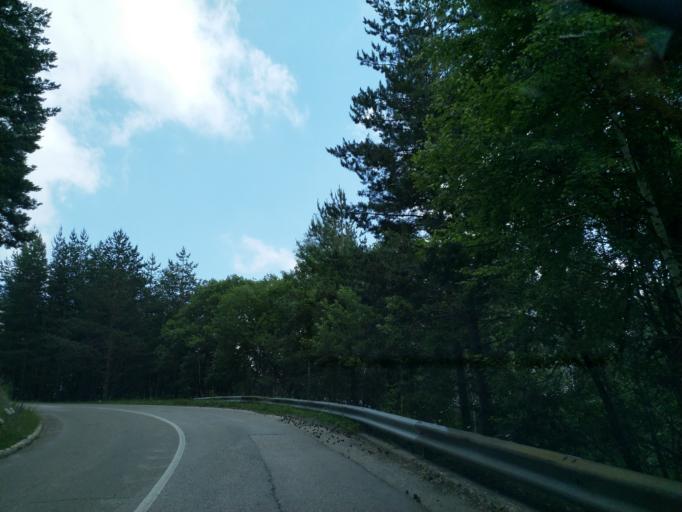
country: XK
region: Mitrovica
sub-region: Komuna e Leposaviqit
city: Leposaviq
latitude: 43.3093
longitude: 20.8619
